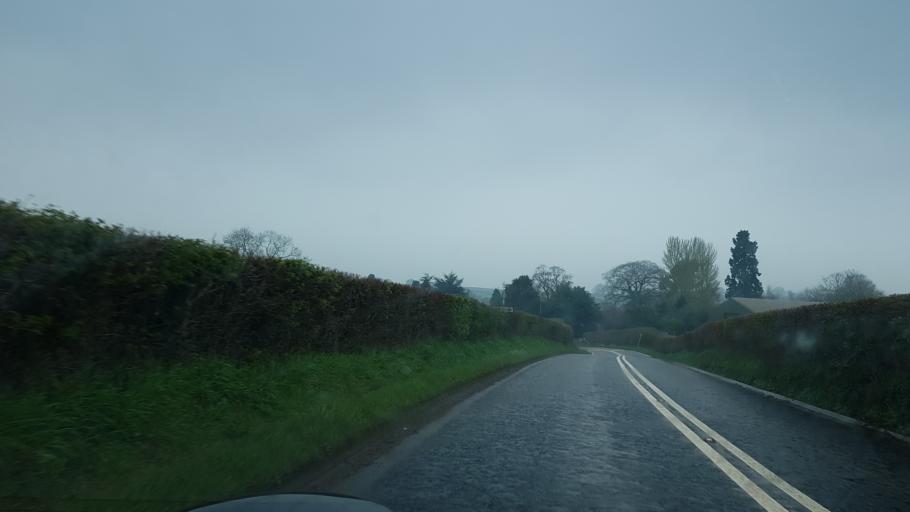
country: GB
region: England
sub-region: Herefordshire
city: Moreton Jeffries
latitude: 52.1450
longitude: -2.5544
